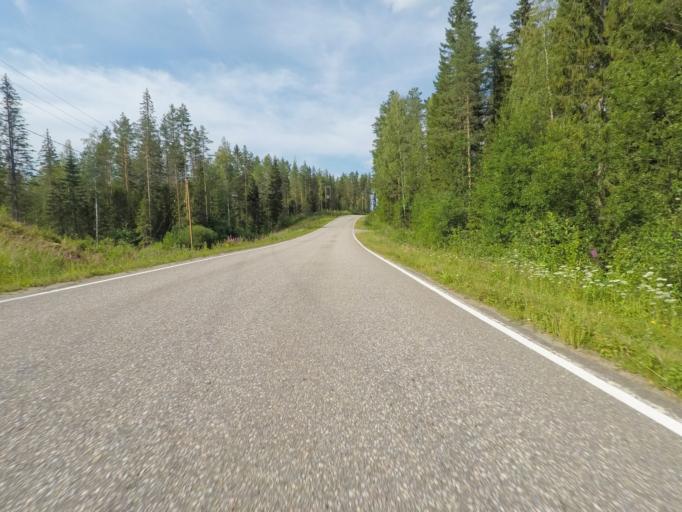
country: FI
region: Southern Savonia
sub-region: Savonlinna
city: Sulkava
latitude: 61.7788
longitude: 28.2389
